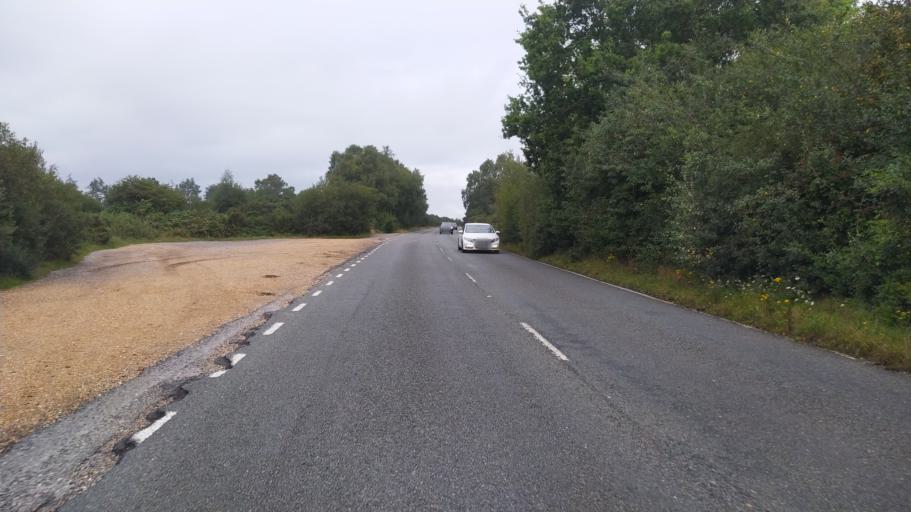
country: GB
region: England
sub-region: Hampshire
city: Sway
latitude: 50.8254
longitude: -1.6514
